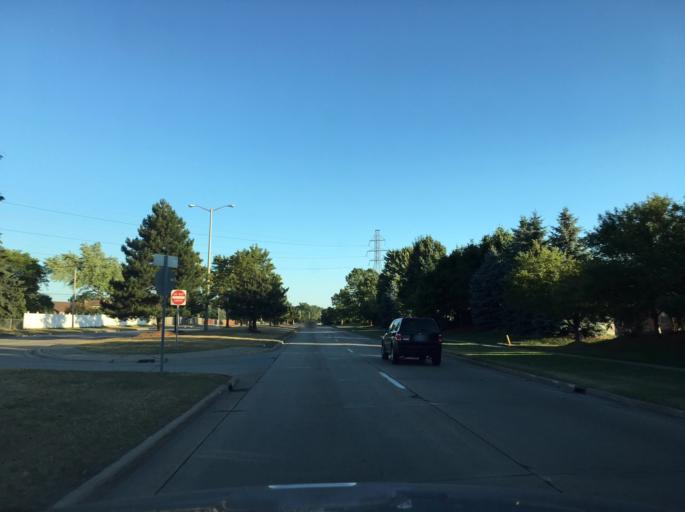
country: US
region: Michigan
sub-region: Macomb County
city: Sterling Heights
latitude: 42.5949
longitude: -82.9917
